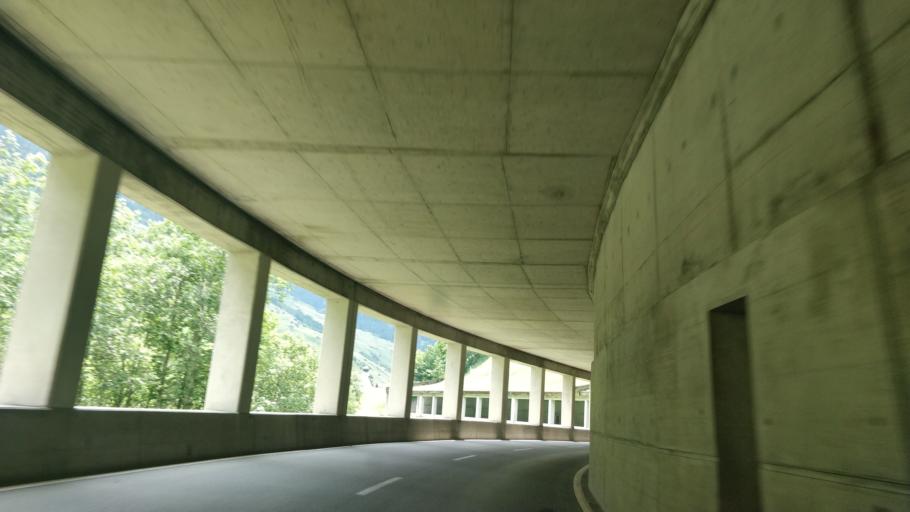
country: CH
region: Grisons
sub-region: Hinterrhein District
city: Hinterrhein
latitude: 46.6306
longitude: 9.1868
